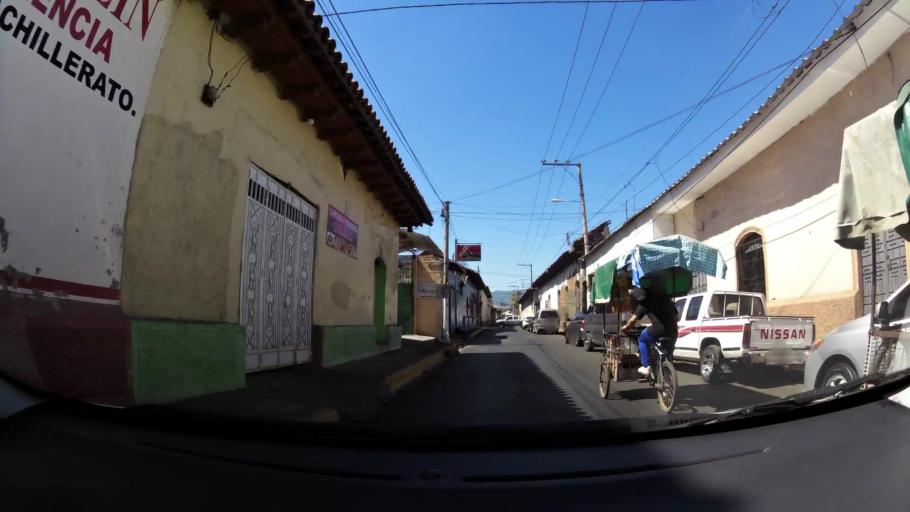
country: SV
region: San Miguel
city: San Miguel
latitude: 13.4852
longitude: -88.1739
